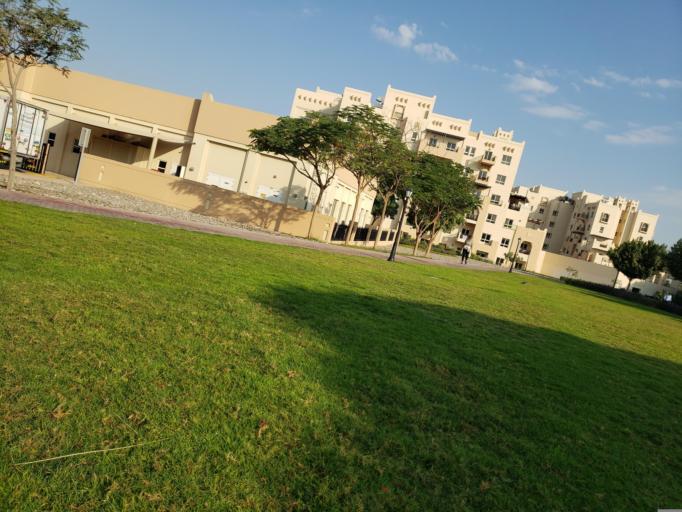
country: AE
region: Dubai
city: Dubai
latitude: 25.0020
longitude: 55.2534
